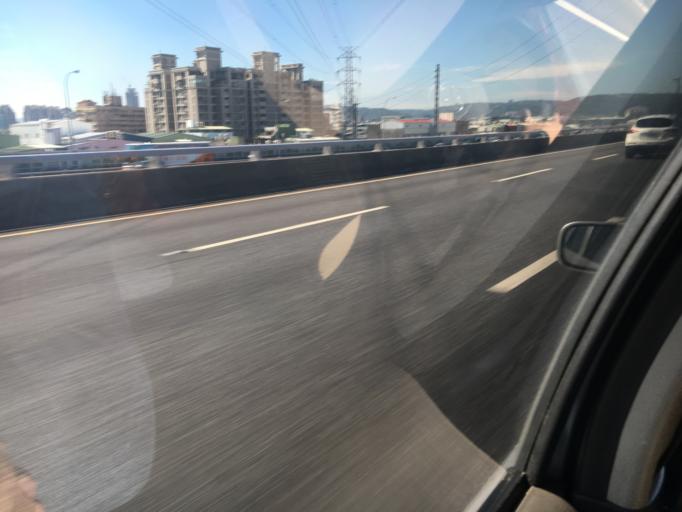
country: TW
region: Taipei
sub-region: Taipei
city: Banqiao
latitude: 25.0760
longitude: 121.4708
